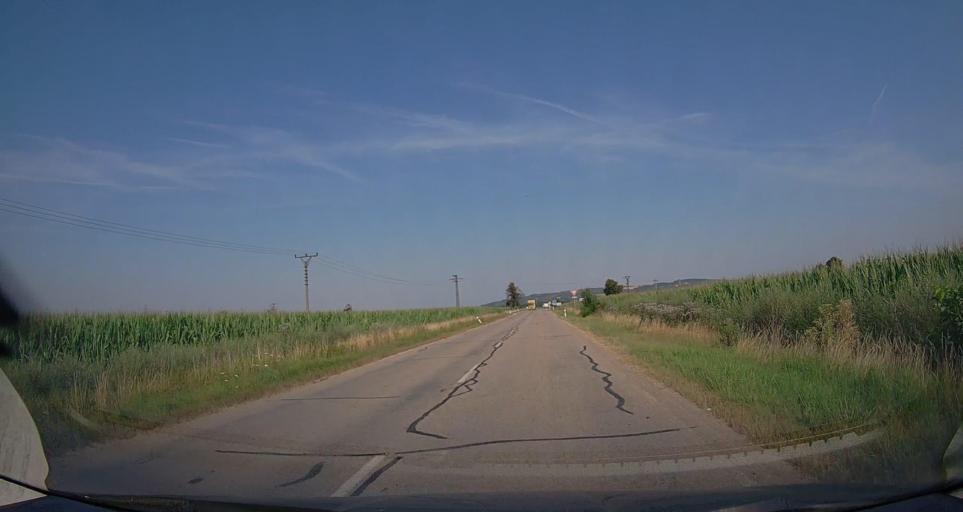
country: CZ
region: South Moravian
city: Hrusovany u Brna
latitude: 49.0477
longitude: 16.5611
